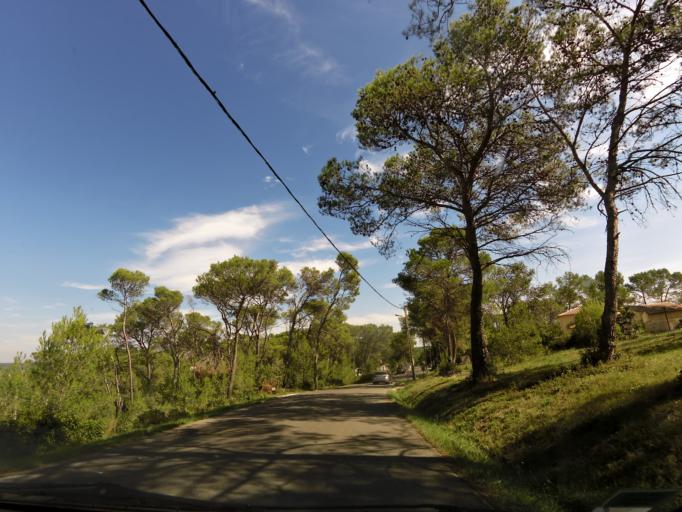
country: FR
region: Languedoc-Roussillon
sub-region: Departement du Gard
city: Langlade
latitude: 43.7991
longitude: 4.2481
